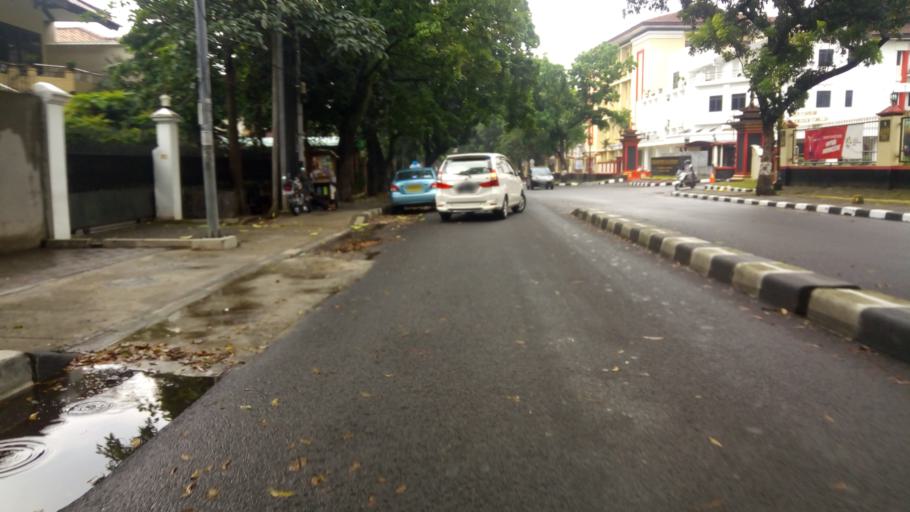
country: ID
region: Jakarta Raya
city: Jakarta
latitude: -6.2444
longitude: 106.8054
